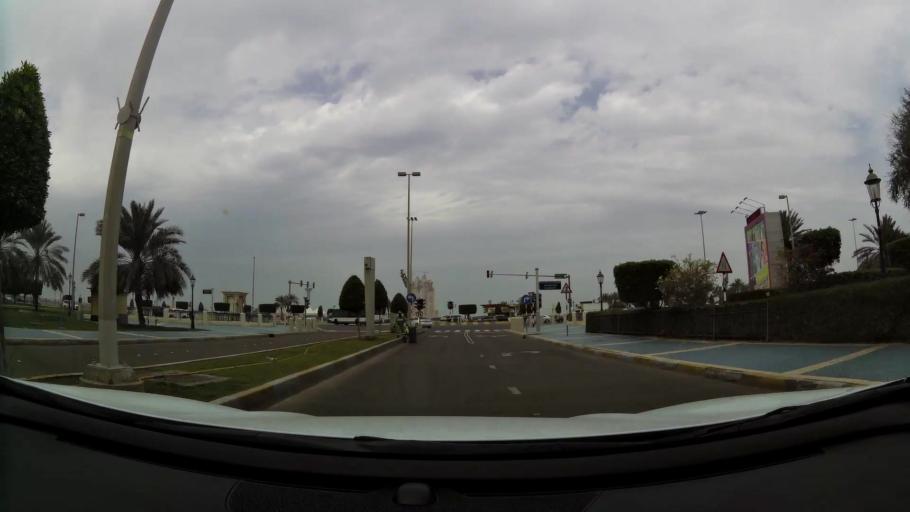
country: AE
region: Abu Dhabi
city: Abu Dhabi
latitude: 24.4677
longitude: 54.3331
